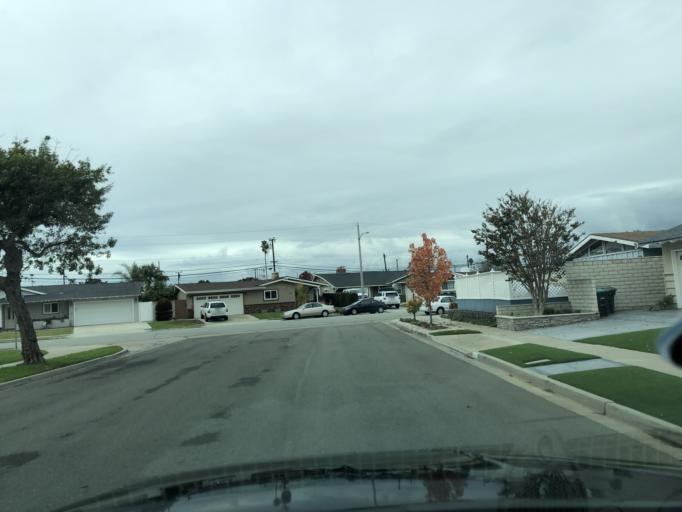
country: US
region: California
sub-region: Orange County
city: Fountain Valley
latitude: 33.6904
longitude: -117.9309
